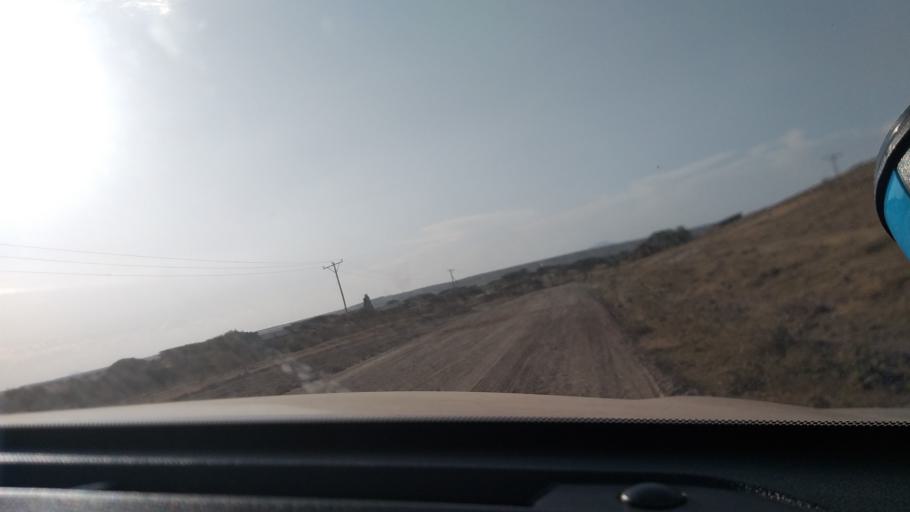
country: ET
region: Oromiya
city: Shashemene
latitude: 7.4986
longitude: 38.6962
